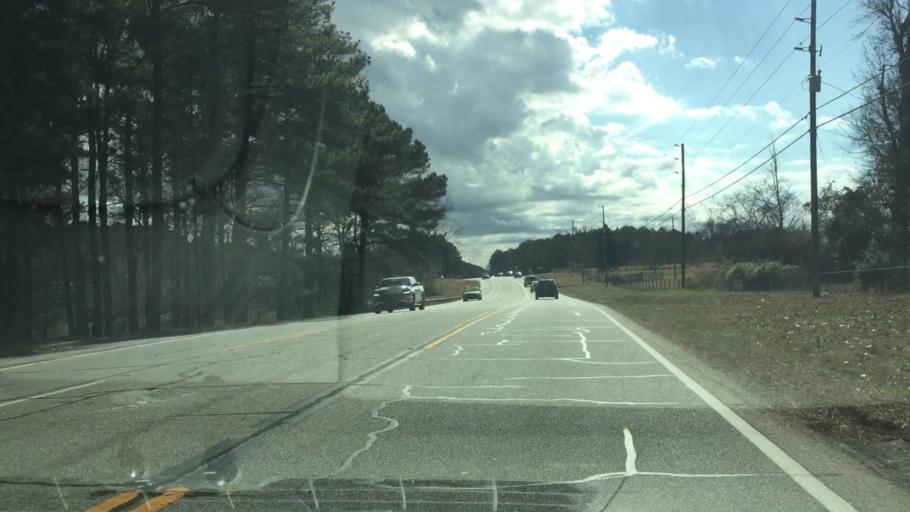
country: US
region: Georgia
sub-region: Henry County
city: McDonough
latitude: 33.4960
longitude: -84.1451
